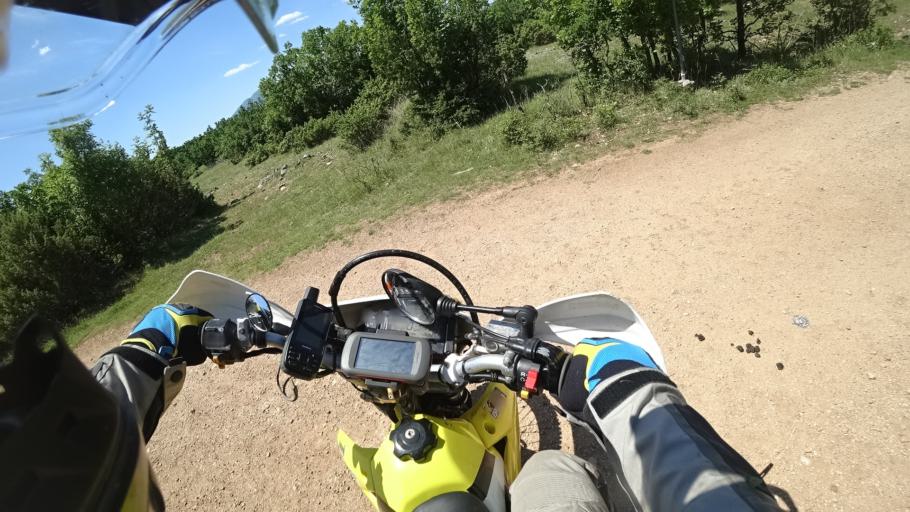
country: HR
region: Sibensko-Kniniska
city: Knin
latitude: 44.0215
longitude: 16.2635
